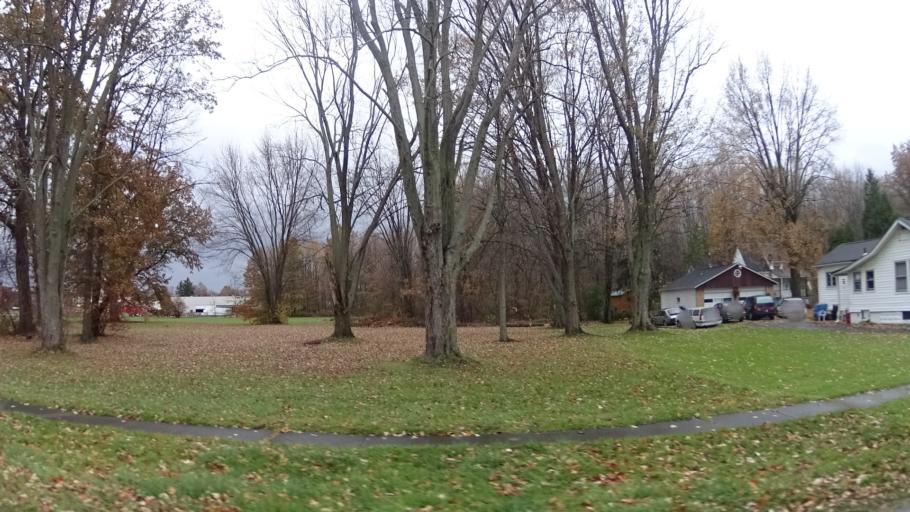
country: US
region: Ohio
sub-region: Lorain County
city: Elyria
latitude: 41.3879
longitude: -82.1315
